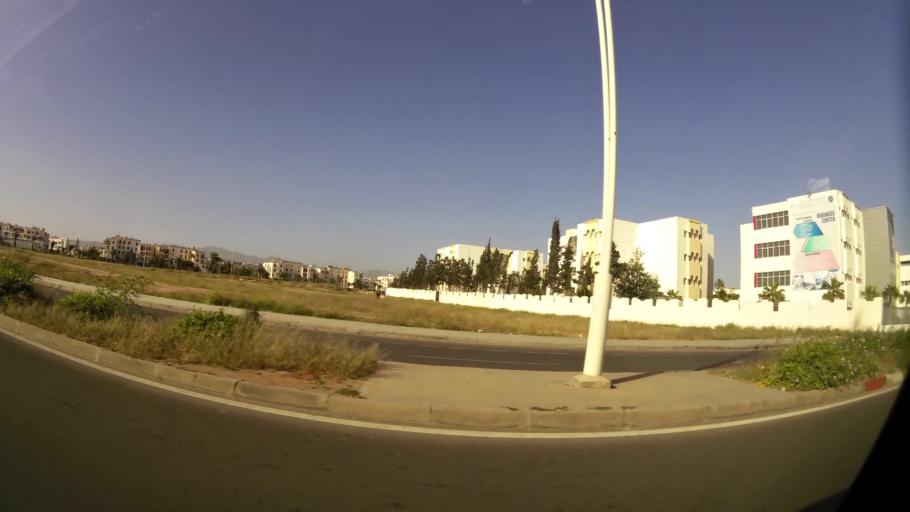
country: MA
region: Oued ed Dahab-Lagouira
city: Dakhla
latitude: 30.4020
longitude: -9.5566
